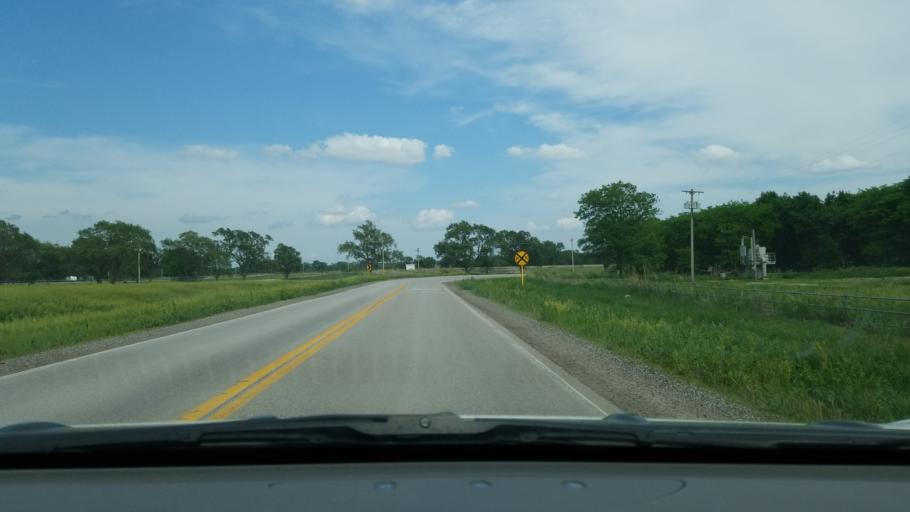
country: US
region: Nebraska
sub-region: Saunders County
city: Ashland
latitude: 41.0598
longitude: -96.3363
